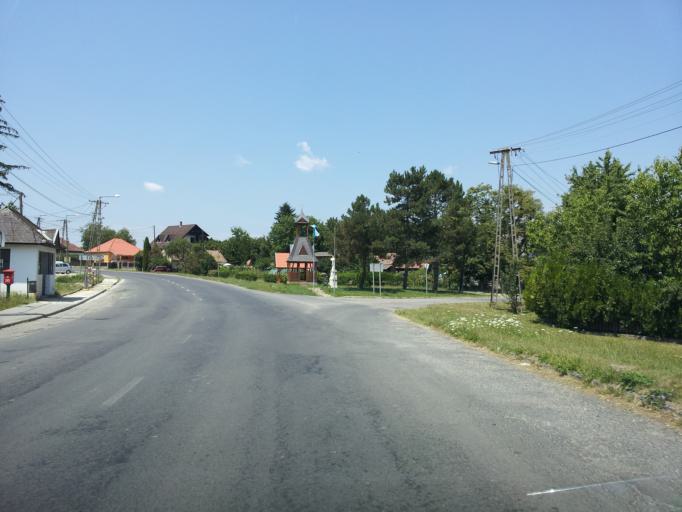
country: HU
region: Zala
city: Zalaegerszeg
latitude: 46.8790
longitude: 16.7324
